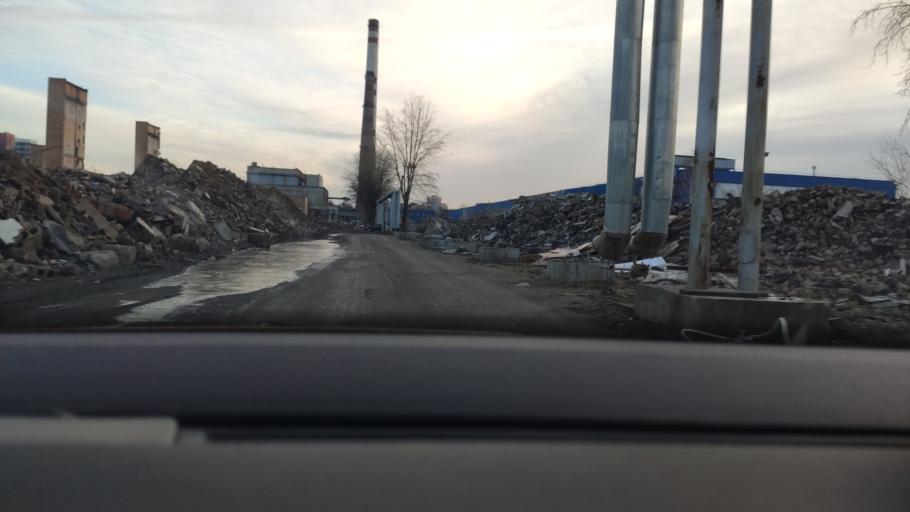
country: RU
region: Moskovskaya
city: Kozhukhovo
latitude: 55.6933
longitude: 37.6473
